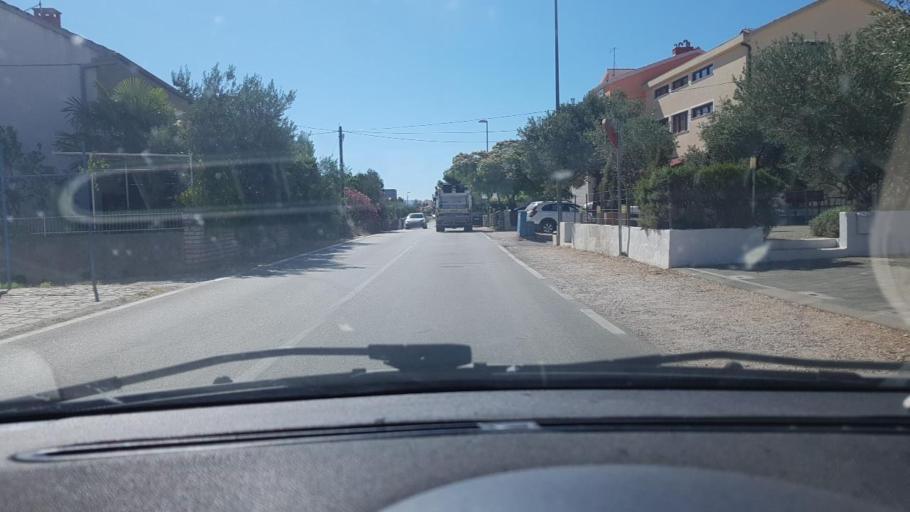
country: HR
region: Sibensko-Kniniska
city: Vodice
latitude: 43.7527
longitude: 15.7915
